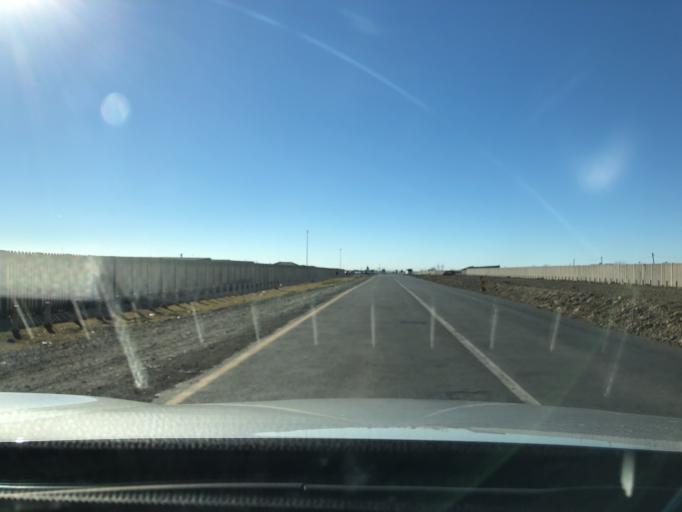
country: ZA
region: Mpumalanga
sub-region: Gert Sibande District Municipality
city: Standerton
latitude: -26.9403
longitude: 29.2048
